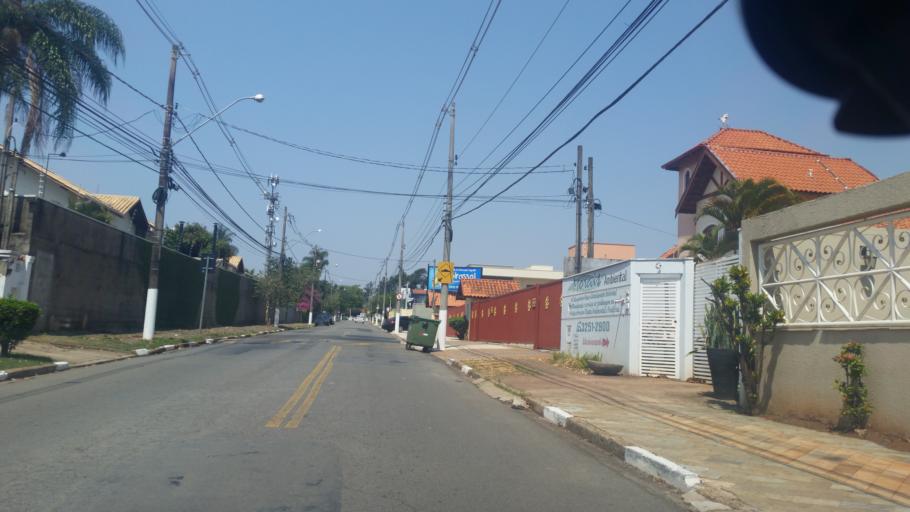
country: BR
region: Sao Paulo
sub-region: Campinas
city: Campinas
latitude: -22.8613
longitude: -47.0527
